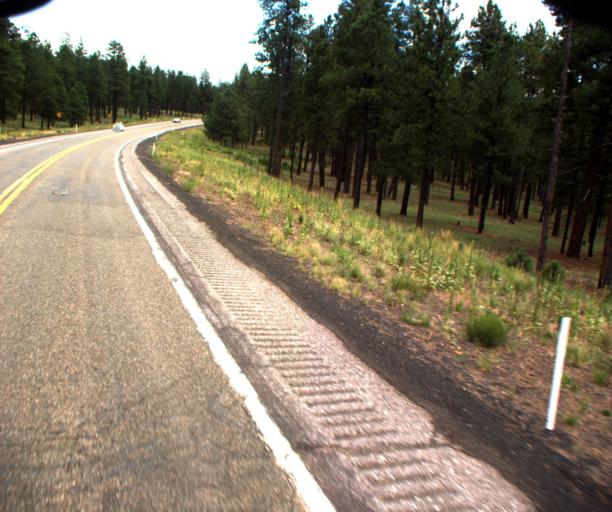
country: US
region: Arizona
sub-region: Coconino County
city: Flagstaff
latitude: 35.2807
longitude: -111.7481
